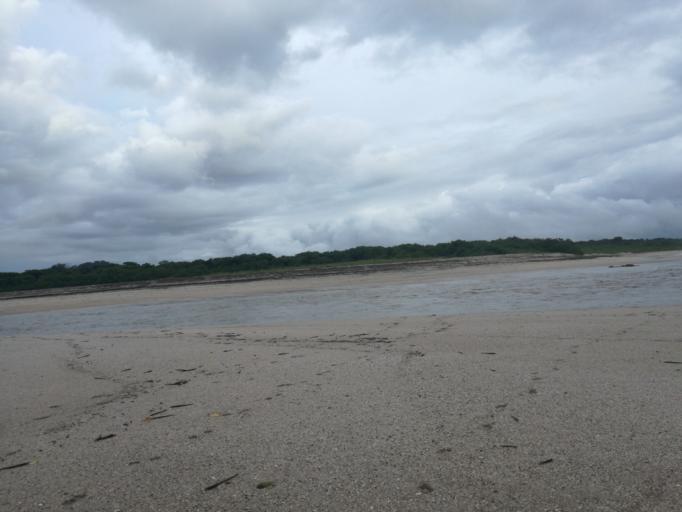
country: CR
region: Guanacaste
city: Santa Cruz
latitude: 10.2851
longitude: -85.8511
